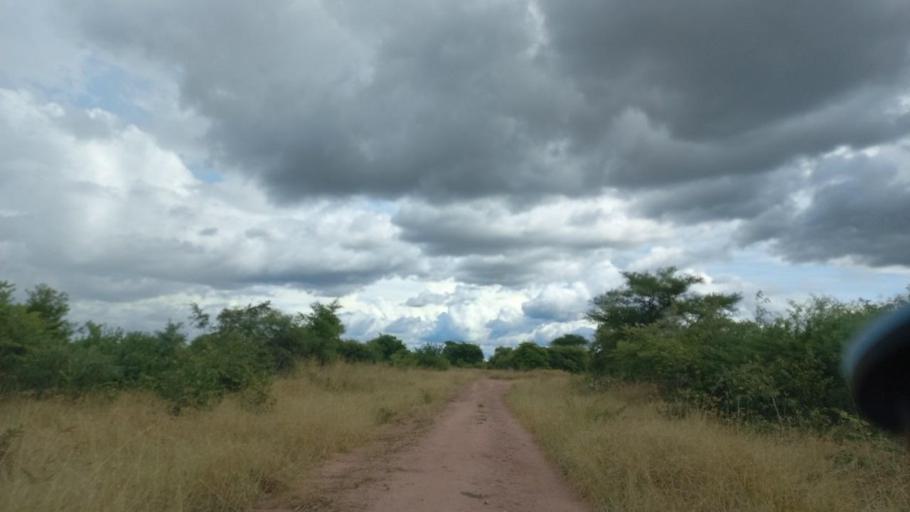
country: ZM
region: Lusaka
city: Luangwa
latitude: -15.6402
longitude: 30.3846
